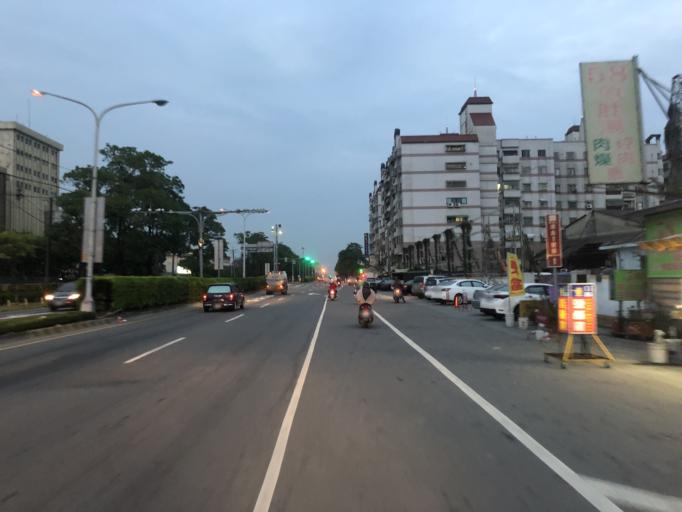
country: TW
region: Taiwan
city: Yujing
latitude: 23.1274
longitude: 120.3189
